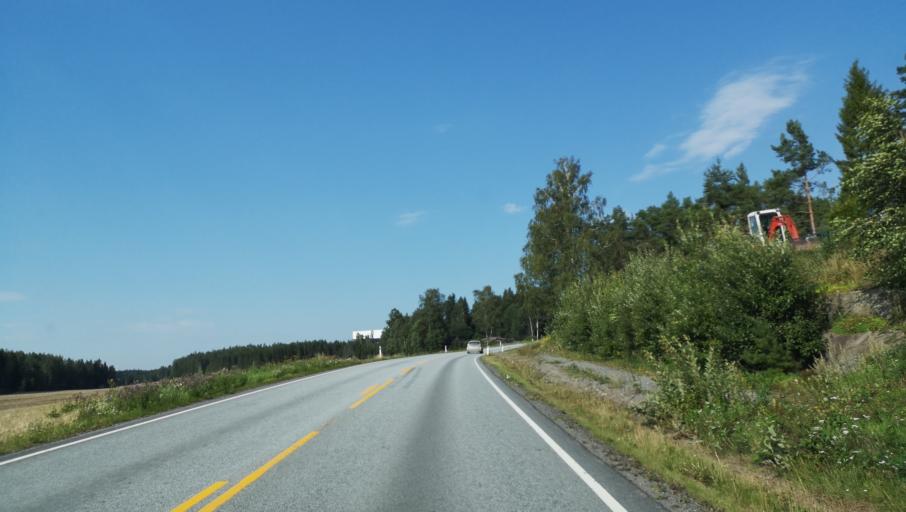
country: NO
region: Ostfold
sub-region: Valer
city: Kirkebygda
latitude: 59.4777
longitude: 10.7909
